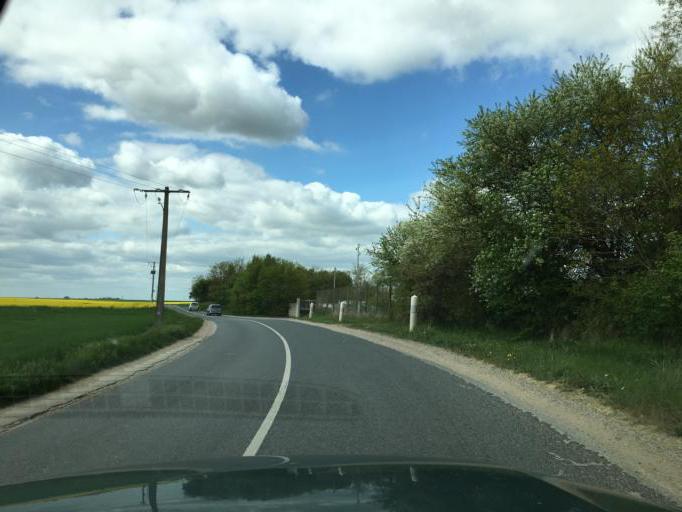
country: FR
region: Centre
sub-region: Departement du Loir-et-Cher
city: Mer
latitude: 47.7345
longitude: 1.4876
